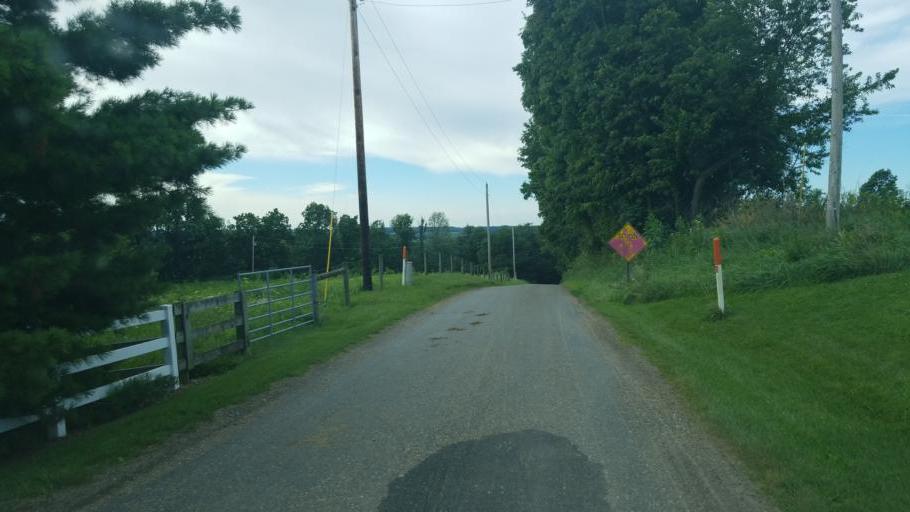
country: US
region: Ohio
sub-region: Holmes County
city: Millersburg
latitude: 40.5002
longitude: -81.8491
